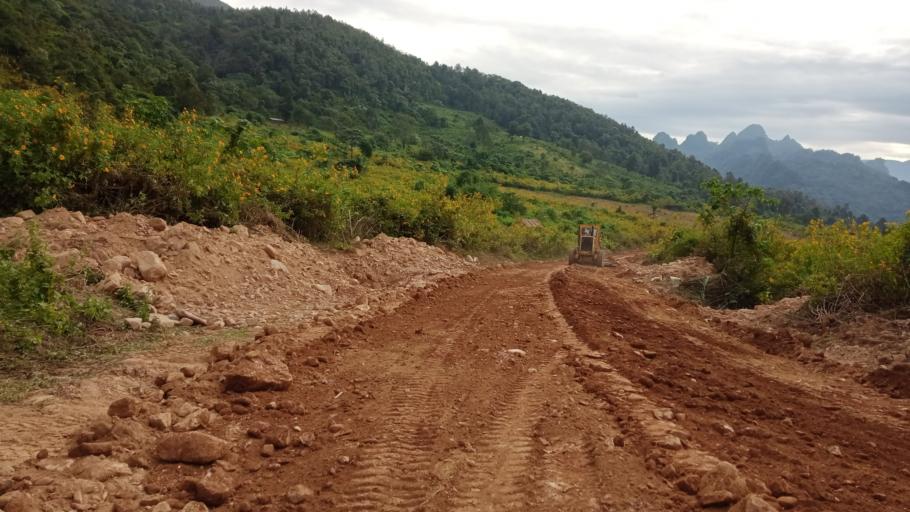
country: LA
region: Xiangkhoang
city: Phonsavan
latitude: 19.1169
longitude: 102.9218
